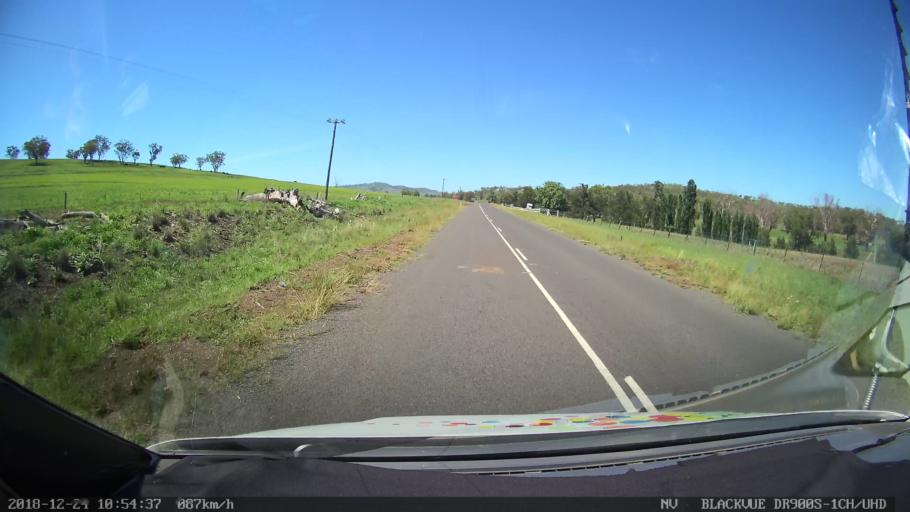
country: AU
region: New South Wales
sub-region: Upper Hunter Shire
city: Merriwa
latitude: -32.0067
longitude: 150.4173
